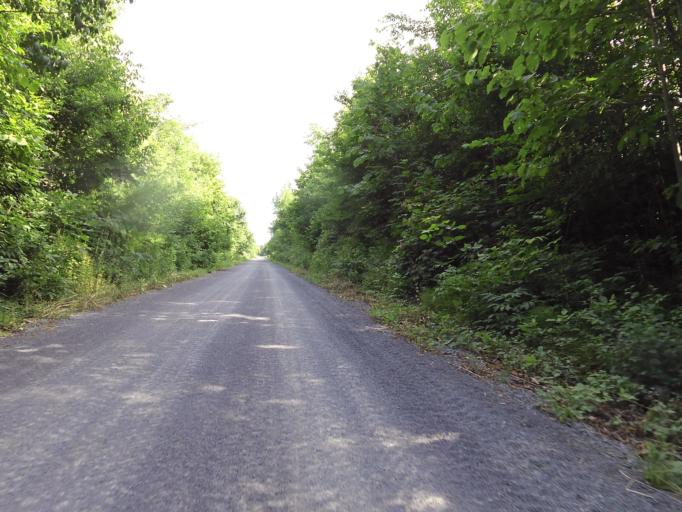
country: CA
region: Ontario
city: Arnprior
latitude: 45.3223
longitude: -76.2870
